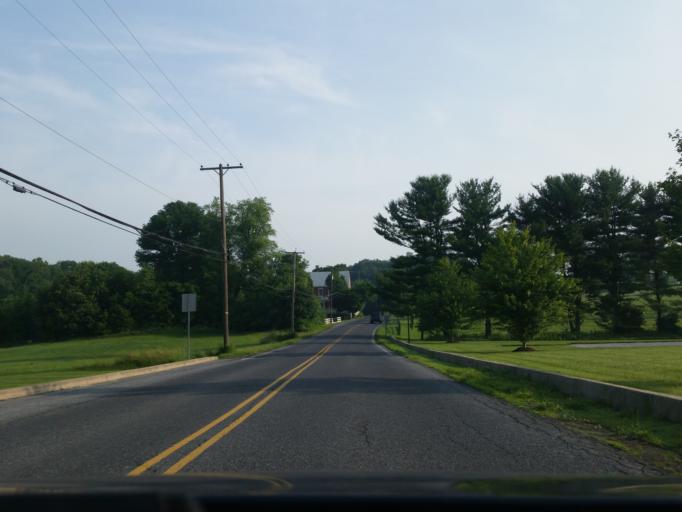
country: US
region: Pennsylvania
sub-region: Lebanon County
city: Annville
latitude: 40.3383
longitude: -76.4995
